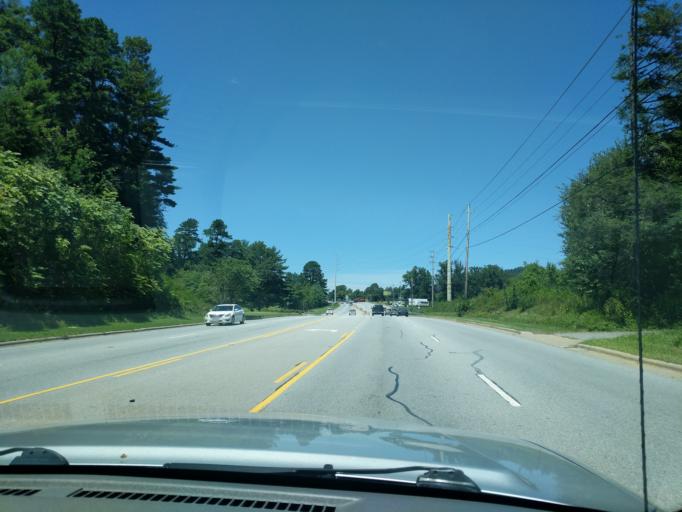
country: US
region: North Carolina
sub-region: Buncombe County
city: Royal Pines
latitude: 35.4564
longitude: -82.5110
